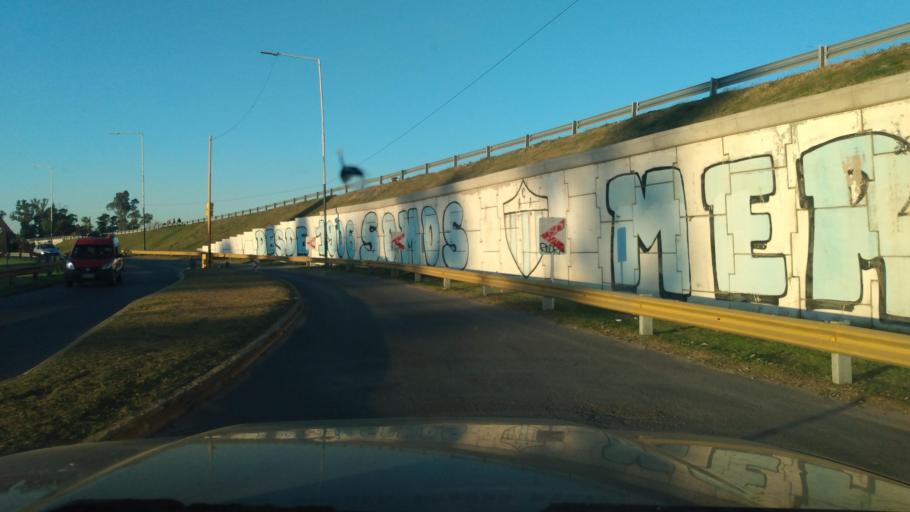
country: AR
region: Buenos Aires
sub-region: Partido de Merlo
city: Merlo
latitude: -34.6430
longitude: -58.7317
